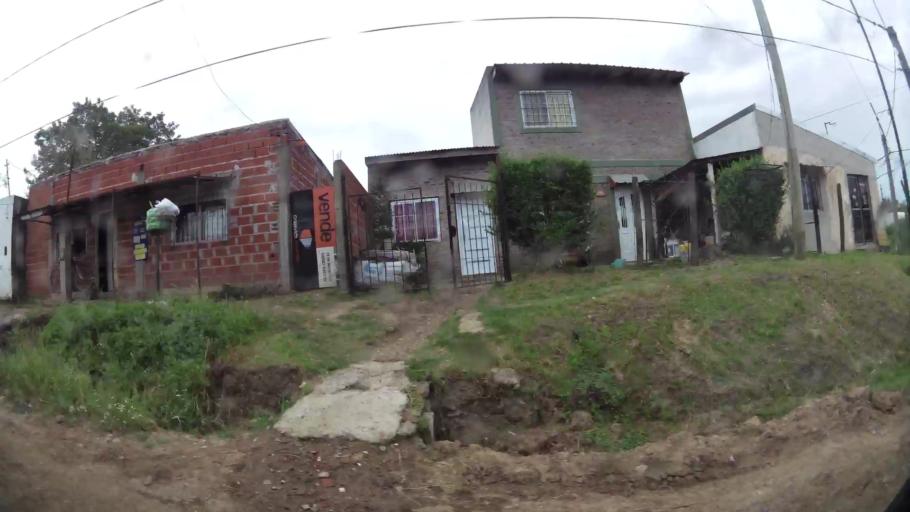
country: AR
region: Buenos Aires
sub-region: Partido de Zarate
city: Zarate
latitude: -34.1146
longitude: -59.0380
